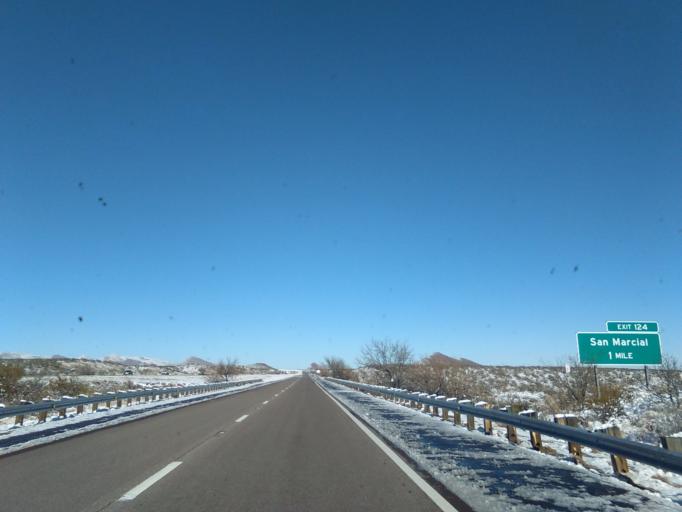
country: US
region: New Mexico
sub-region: Socorro County
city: Socorro
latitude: 33.7238
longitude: -107.0254
